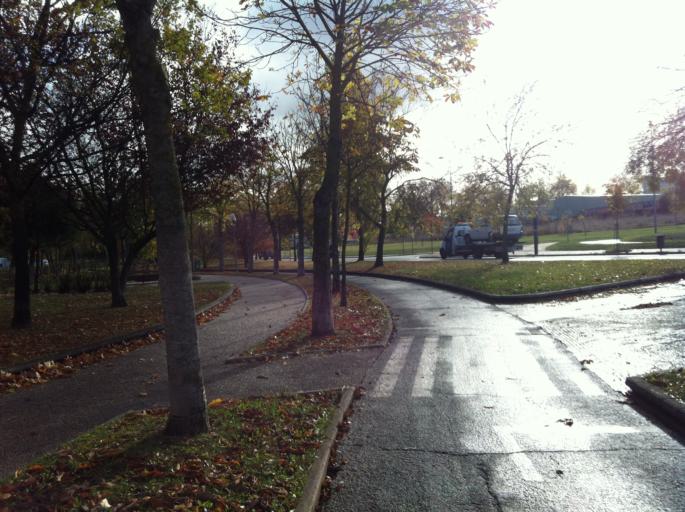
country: ES
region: Basque Country
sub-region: Provincia de Alava
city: Gasteiz / Vitoria
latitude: 42.8347
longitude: -2.6682
